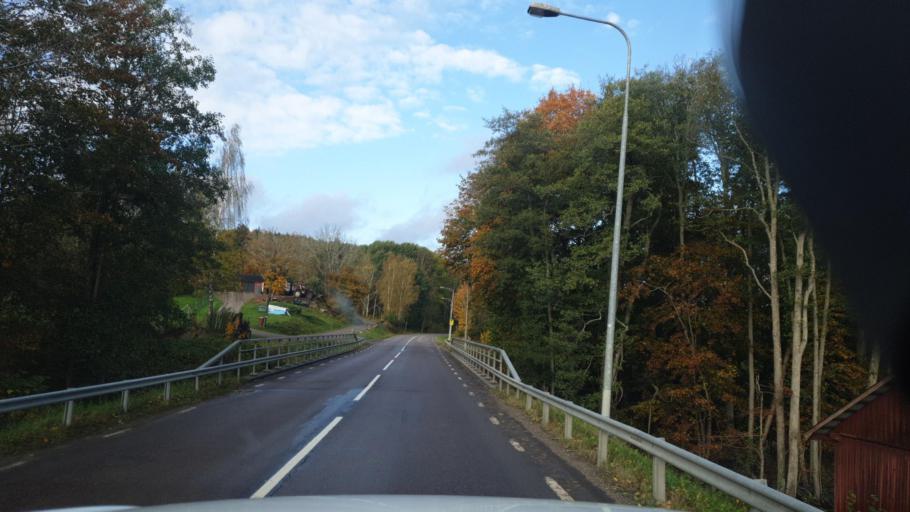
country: SE
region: Vaermland
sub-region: Arvika Kommun
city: Arvika
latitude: 59.4865
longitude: 12.6918
